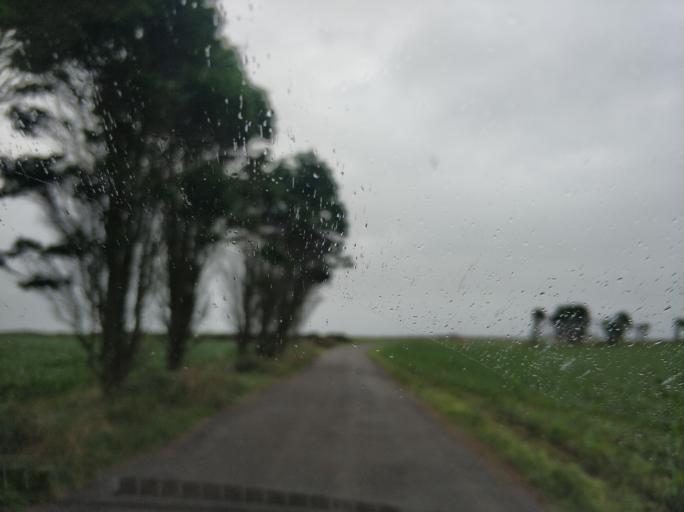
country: ES
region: Asturias
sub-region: Province of Asturias
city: Tineo
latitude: 43.5662
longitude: -6.4704
